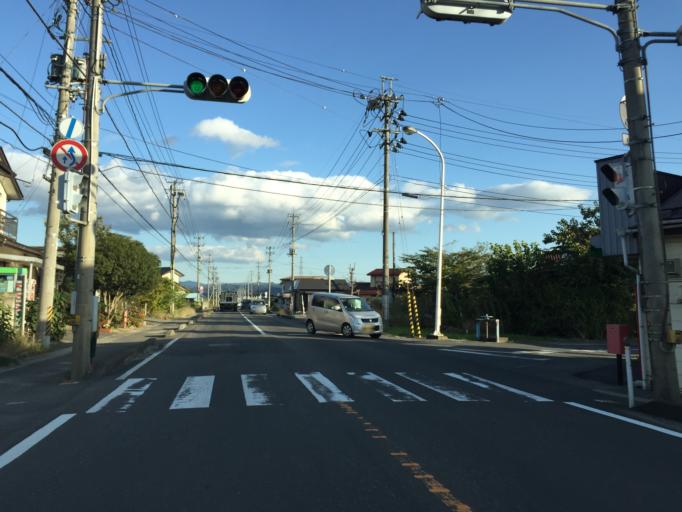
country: JP
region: Fukushima
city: Fukushima-shi
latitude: 37.8187
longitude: 140.4529
